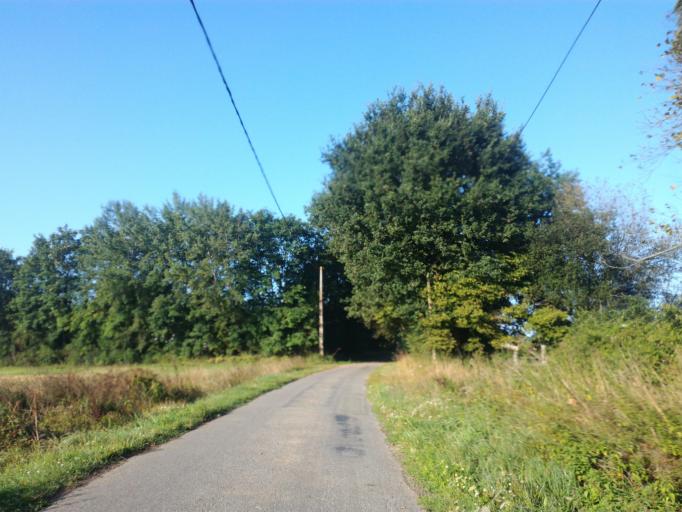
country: FR
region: Brittany
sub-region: Departement d'Ille-et-Vilaine
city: Fouillard
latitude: 48.1444
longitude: -1.5973
